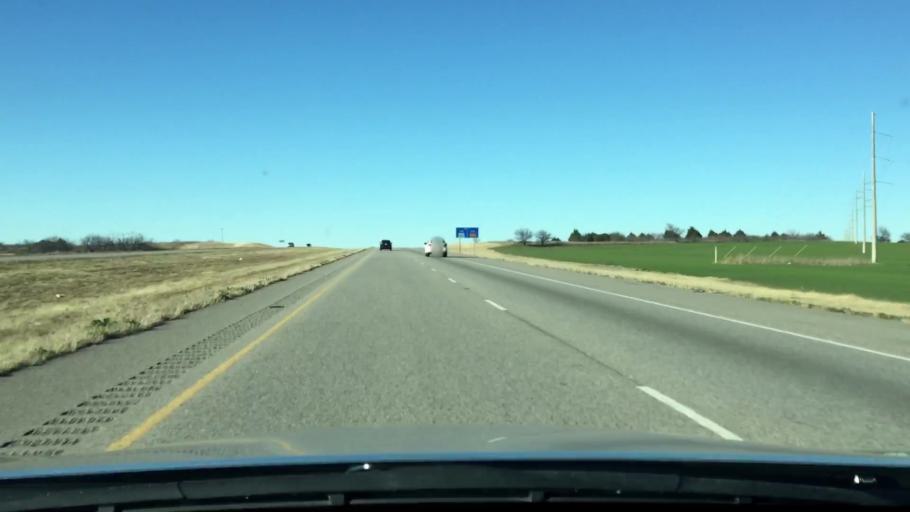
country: US
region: Texas
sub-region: Hill County
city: Itasca
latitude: 32.1386
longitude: -97.1216
